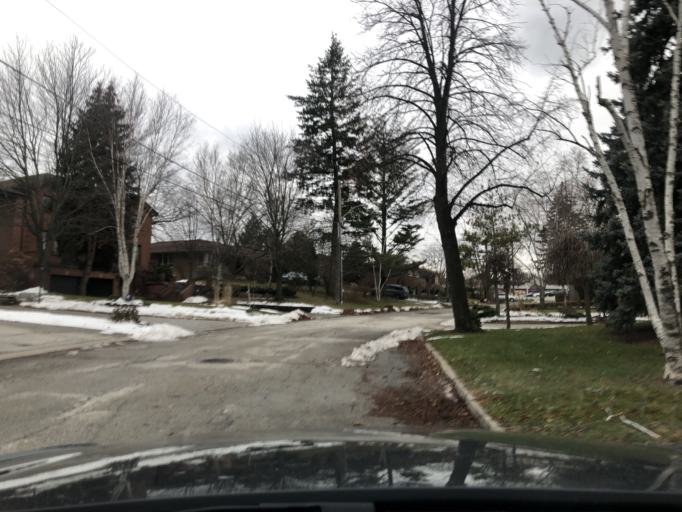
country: CA
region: Ontario
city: Etobicoke
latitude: 43.6923
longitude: -79.5295
